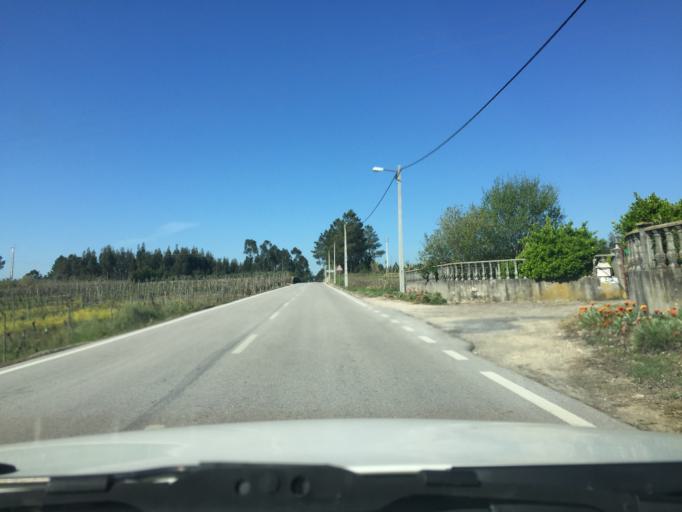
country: PT
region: Coimbra
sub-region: Cantanhede
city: Cantanhede
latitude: 40.4208
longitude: -8.5399
